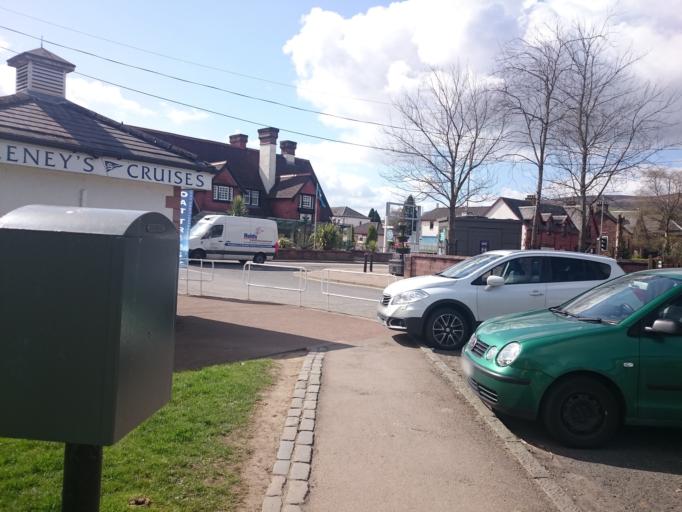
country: GB
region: Scotland
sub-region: West Dunbartonshire
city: Balloch
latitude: 56.0033
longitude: -4.5832
